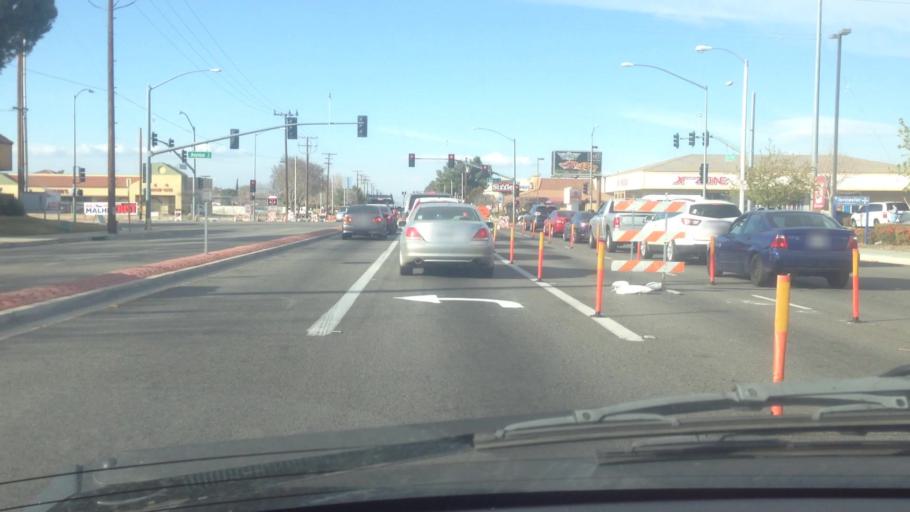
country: US
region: California
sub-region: Los Angeles County
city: Lancaster
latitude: 34.6887
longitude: -118.1657
